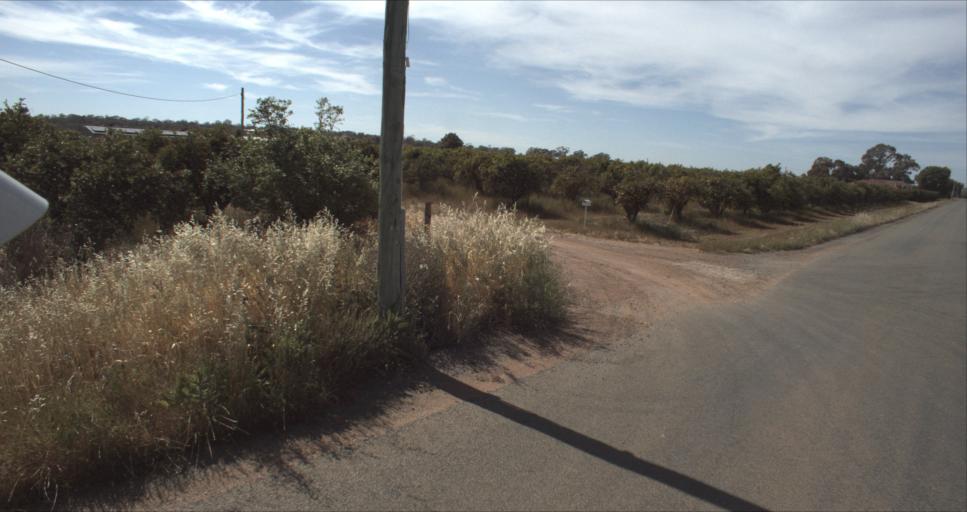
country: AU
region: New South Wales
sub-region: Leeton
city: Leeton
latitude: -34.5835
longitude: 146.4707
